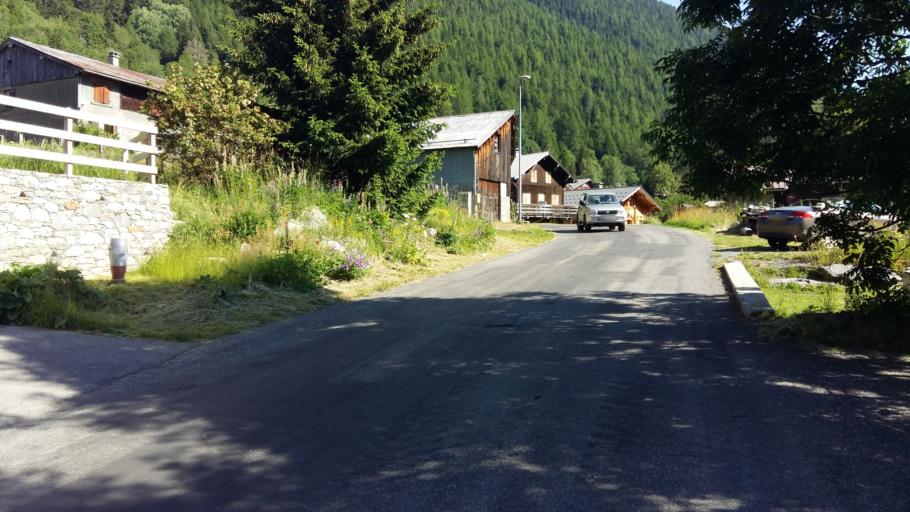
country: FR
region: Rhone-Alpes
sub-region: Departement de la Haute-Savoie
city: Chamonix-Mont-Blanc
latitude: 46.0224
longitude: 6.9185
